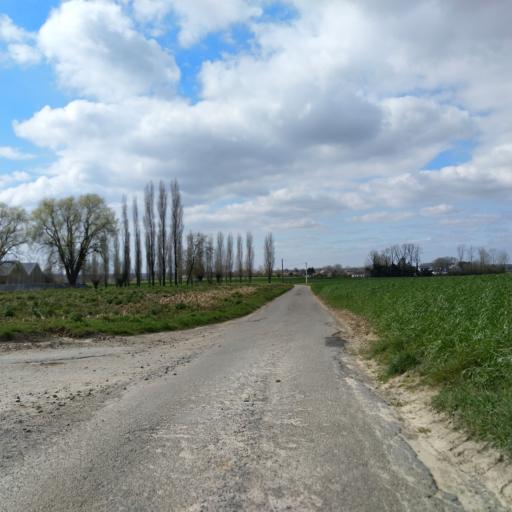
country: BE
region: Wallonia
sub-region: Province du Hainaut
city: Jurbise
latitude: 50.5391
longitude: 3.9513
